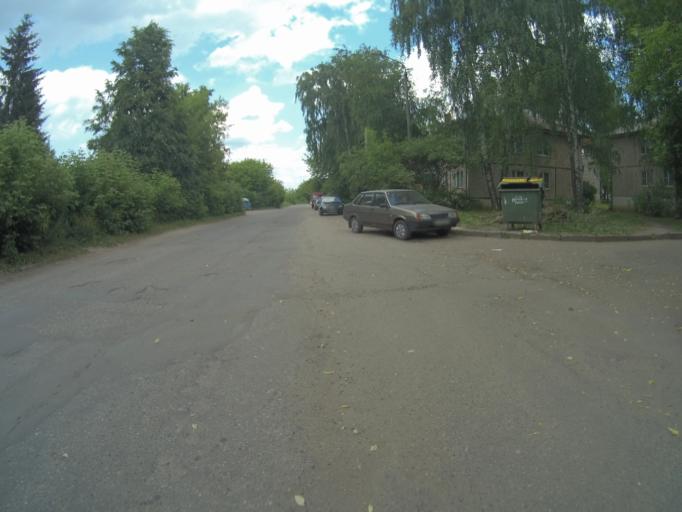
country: RU
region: Vladimir
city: Suzdal'
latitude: 56.4419
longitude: 40.4606
